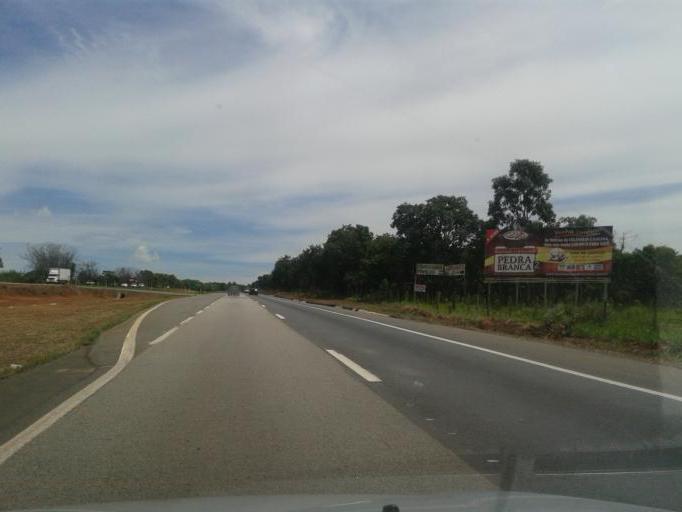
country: BR
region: Goias
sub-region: Hidrolandia
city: Hidrolandia
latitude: -17.0611
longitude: -49.2254
